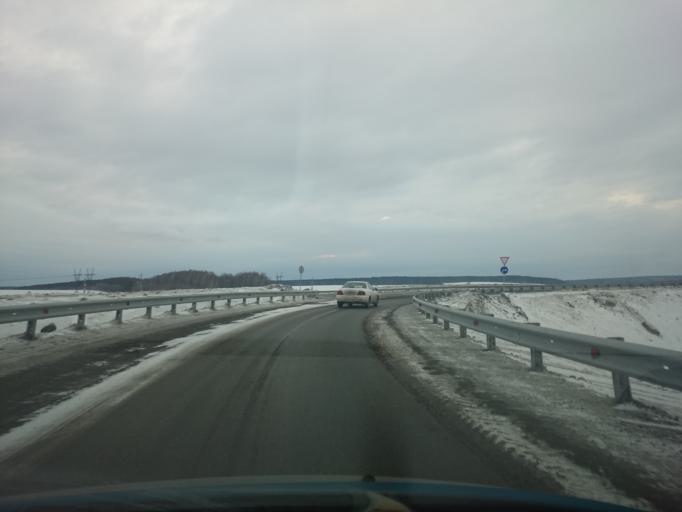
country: RU
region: Sverdlovsk
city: Achit
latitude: 56.7889
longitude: 57.8840
